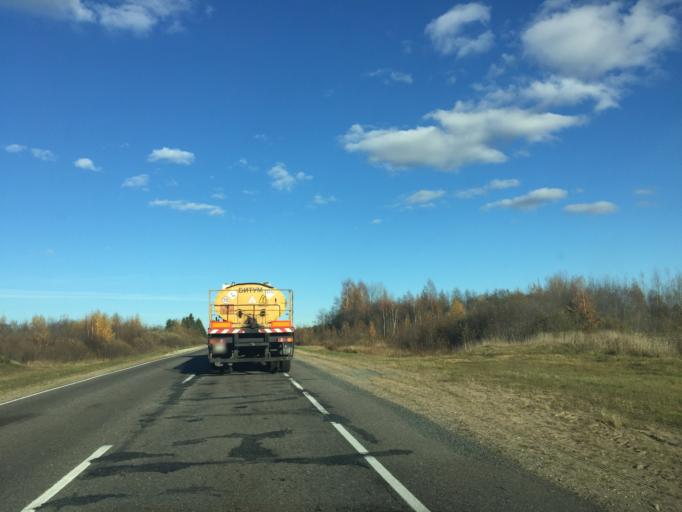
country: BY
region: Vitebsk
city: Dzisna
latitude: 55.2770
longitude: 28.1608
